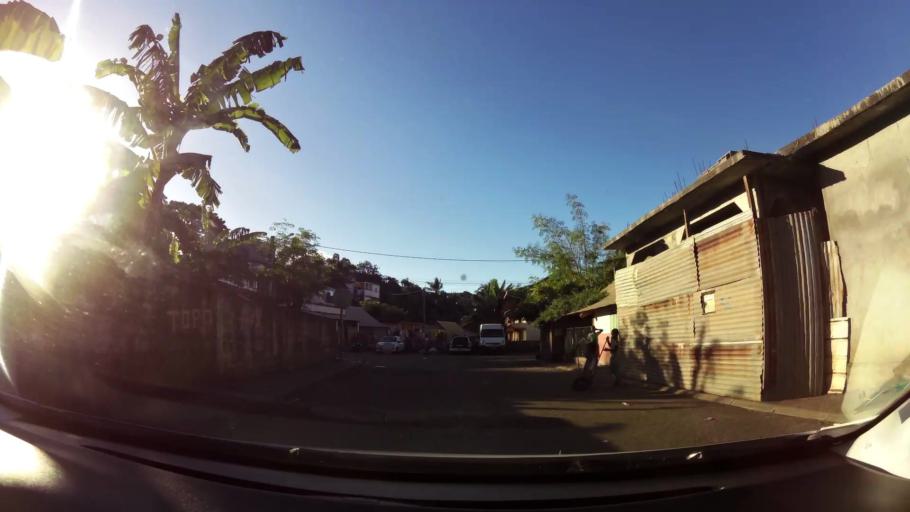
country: YT
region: Koungou
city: Koungou
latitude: -12.7352
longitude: 45.2065
